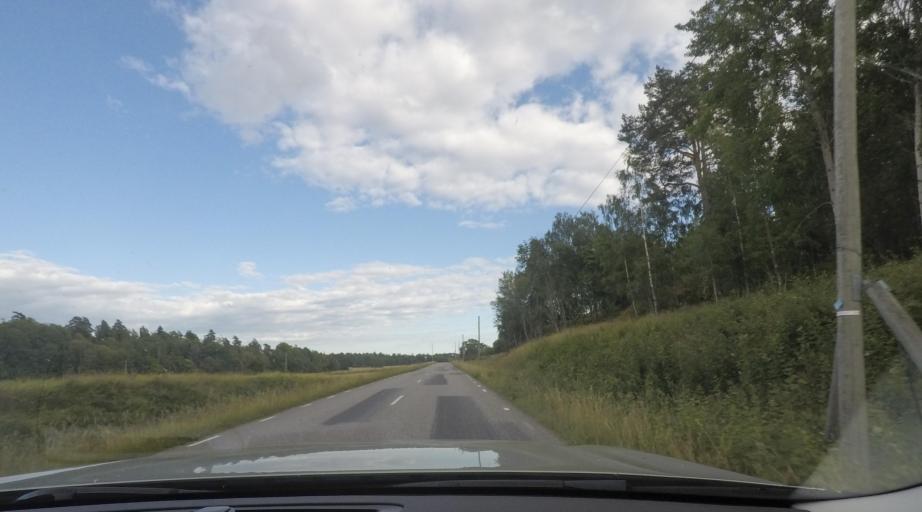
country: SE
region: Soedermanland
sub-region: Trosa Kommun
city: Trosa
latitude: 58.9856
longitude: 17.6811
